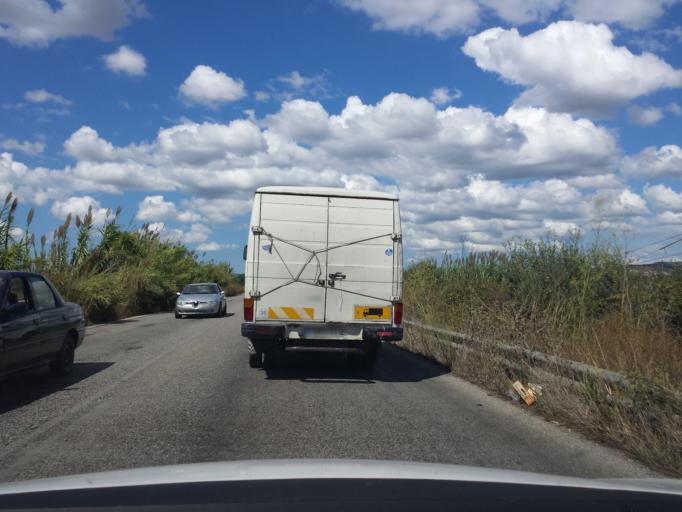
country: GR
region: West Greece
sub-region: Nomos Ileias
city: Epitalion
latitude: 37.6462
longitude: 21.4743
